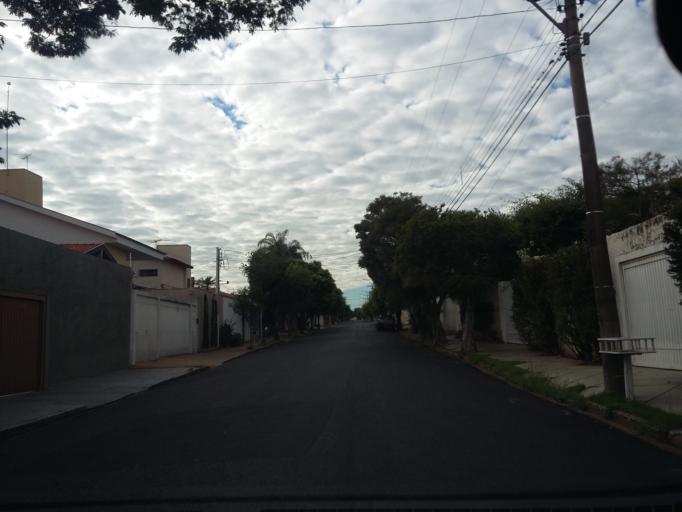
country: BR
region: Sao Paulo
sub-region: Sao Jose Do Rio Preto
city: Sao Jose do Rio Preto
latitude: -20.8396
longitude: -49.4068
